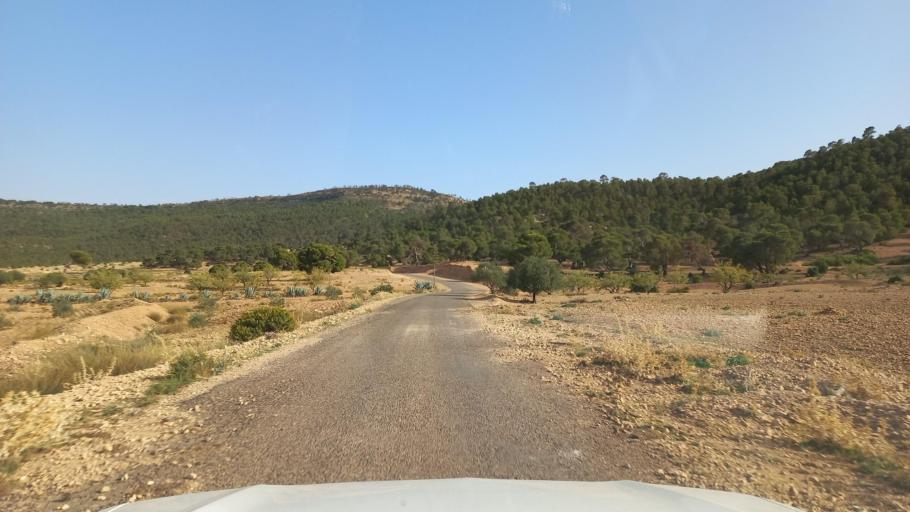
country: TN
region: Al Qasrayn
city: Kasserine
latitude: 35.3352
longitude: 8.8399
